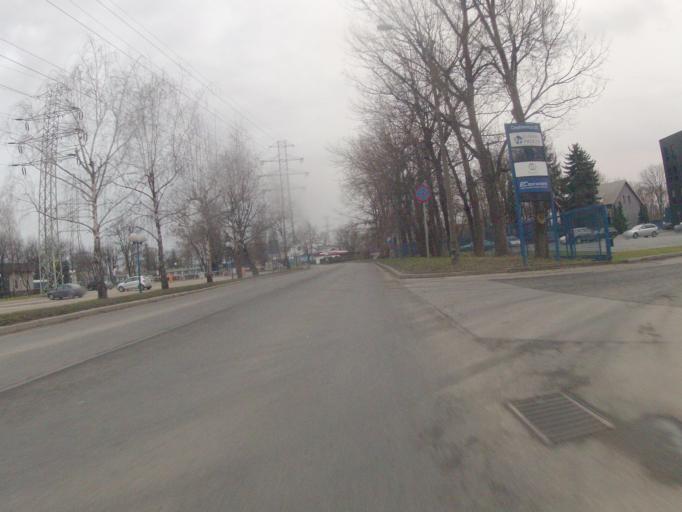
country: PL
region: Lesser Poland Voivodeship
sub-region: Krakow
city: Krakow
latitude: 50.0531
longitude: 20.0026
